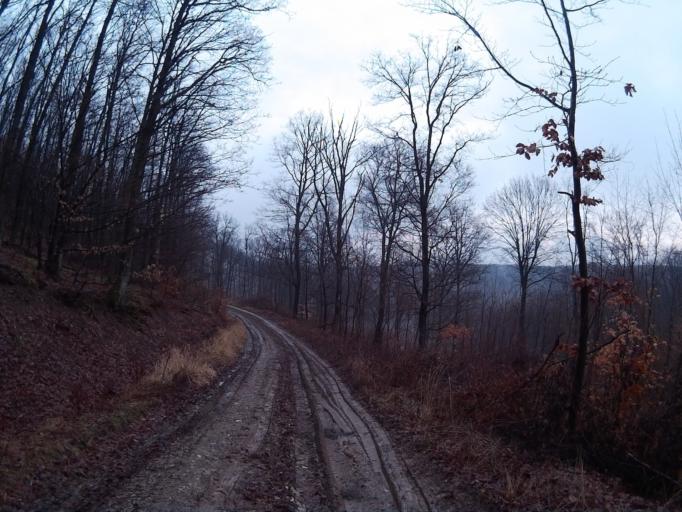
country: HU
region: Borsod-Abauj-Zemplen
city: Satoraljaujhely
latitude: 48.4200
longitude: 21.5694
